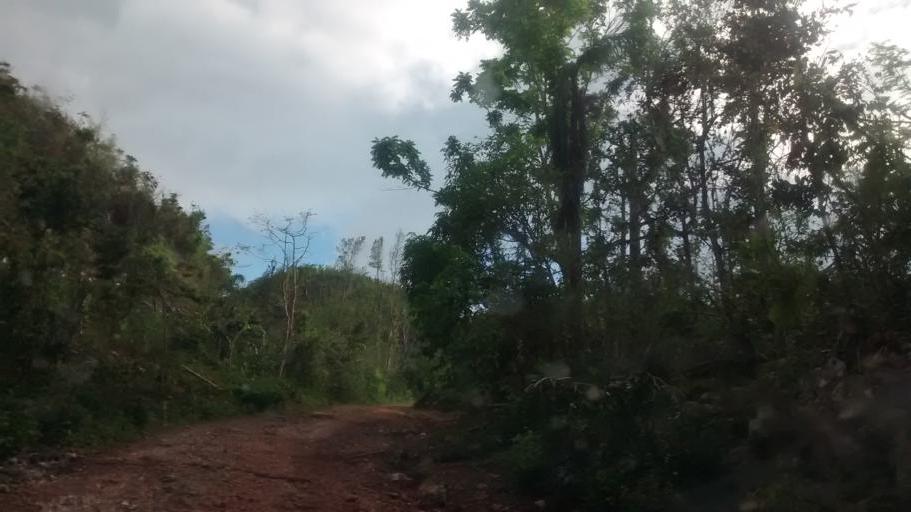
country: HT
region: Grandans
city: Corail
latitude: 18.5105
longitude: -73.7832
